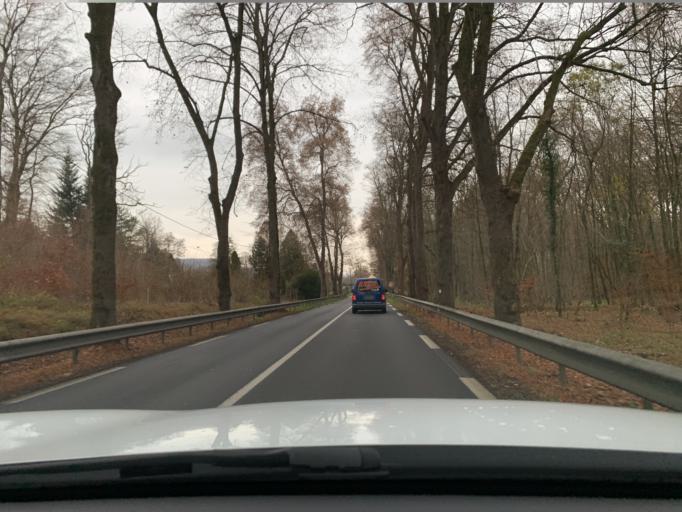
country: FR
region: Lorraine
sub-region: Departement de la Moselle
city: Grosbliederstroff
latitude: 49.1877
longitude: 7.0283
